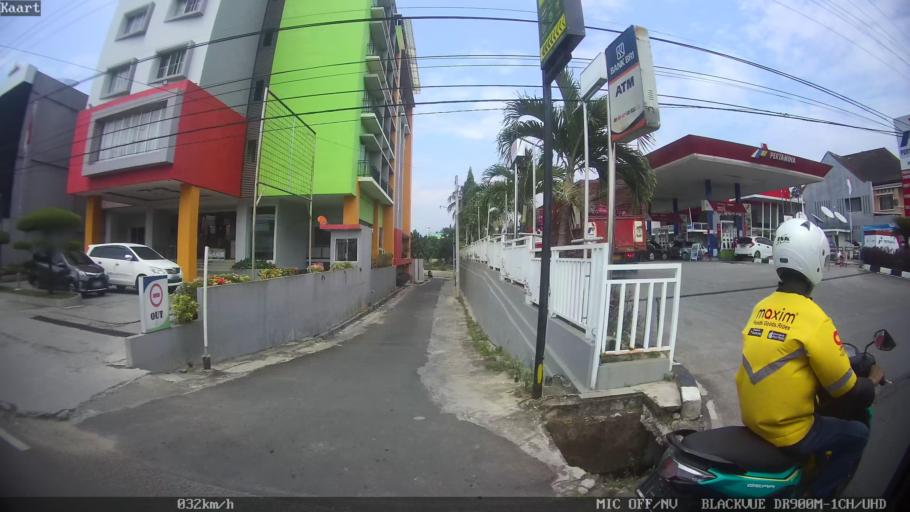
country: ID
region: Lampung
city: Bandarlampung
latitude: -5.4327
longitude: 105.2534
